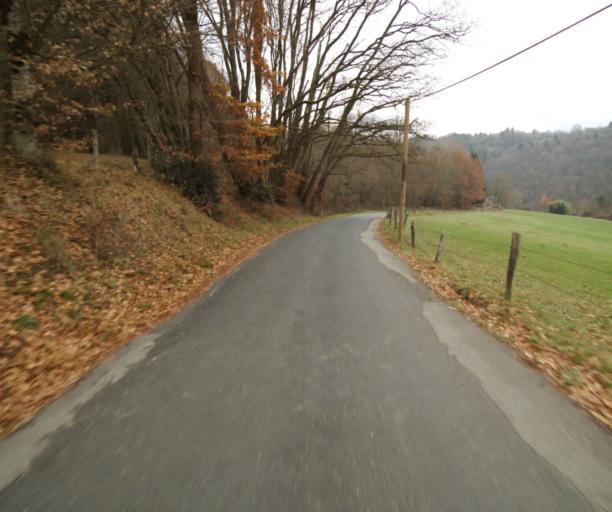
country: FR
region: Limousin
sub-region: Departement de la Correze
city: Tulle
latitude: 45.2448
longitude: 1.7380
